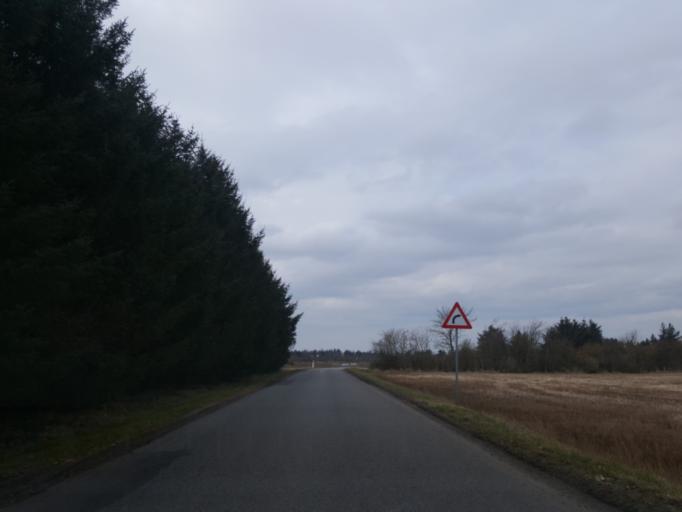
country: DK
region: Central Jutland
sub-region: Holstebro Kommune
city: Ulfborg
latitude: 56.3692
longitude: 8.2313
